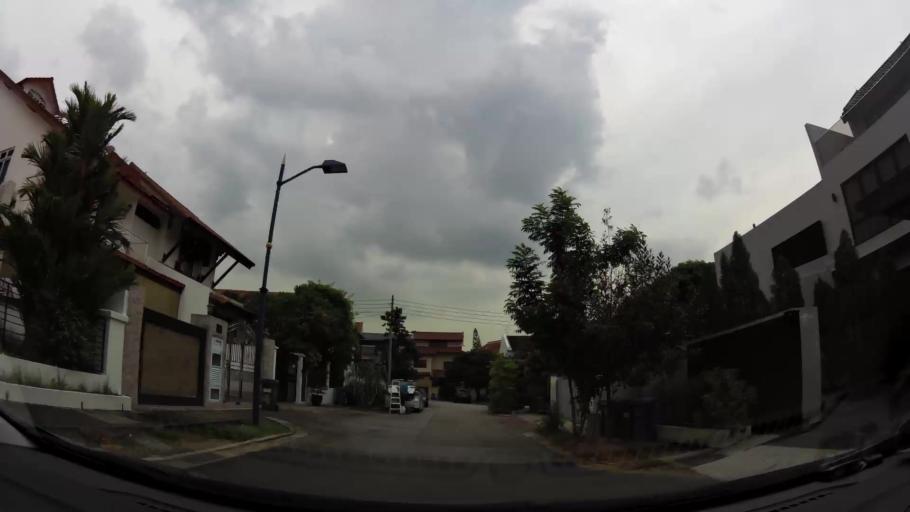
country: SG
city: Singapore
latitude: 1.3667
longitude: 103.8679
